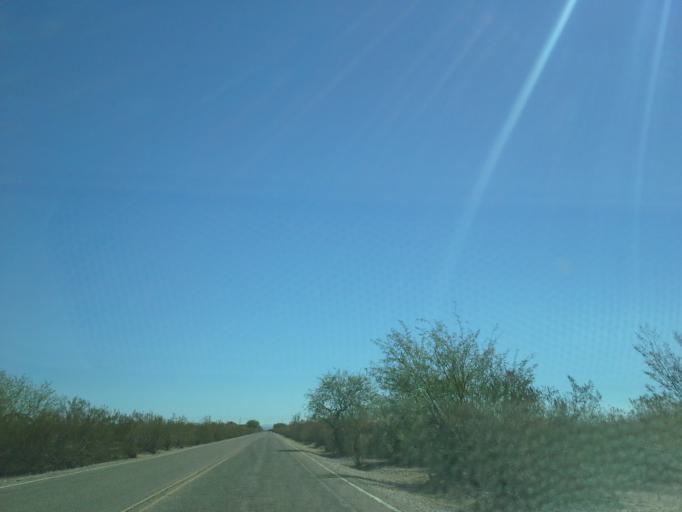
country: US
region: Arizona
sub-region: Pinal County
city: Coolidge
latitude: 32.9954
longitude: -111.5299
